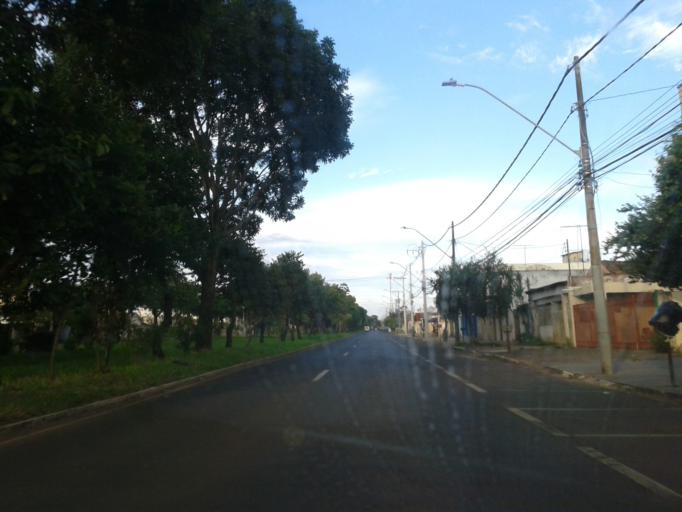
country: BR
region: Minas Gerais
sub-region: Araguari
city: Araguari
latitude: -18.6408
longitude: -48.2036
